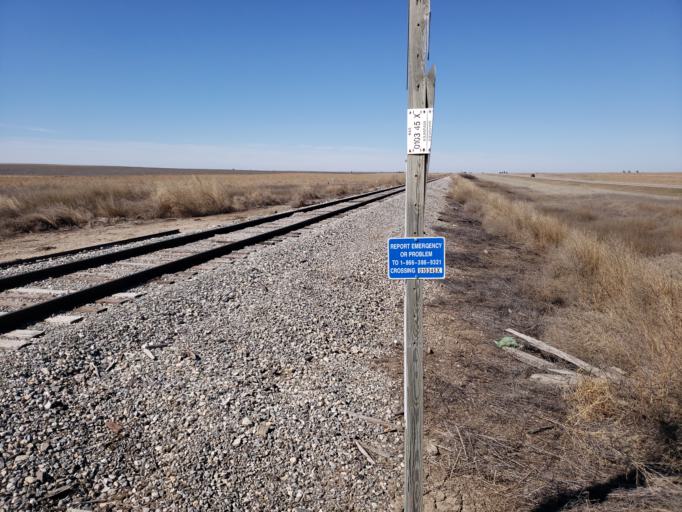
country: US
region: Kansas
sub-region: Ness County
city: Ness City
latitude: 38.4517
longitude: -99.9354
